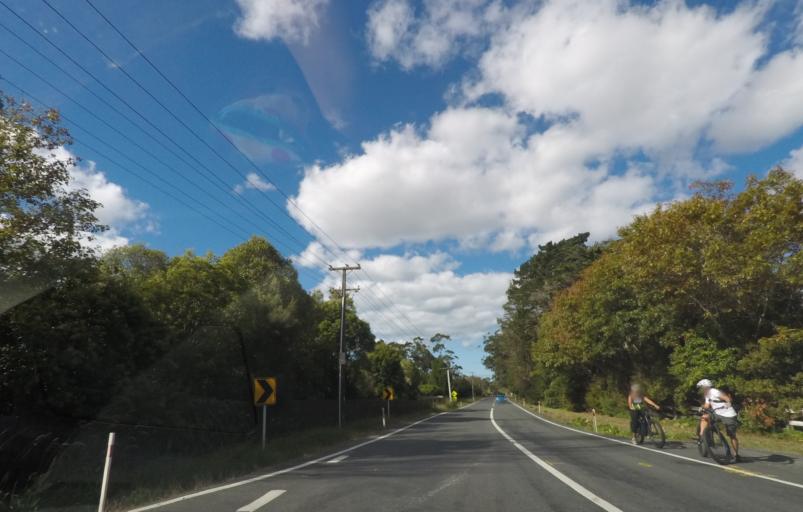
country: NZ
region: Auckland
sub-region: Auckland
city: Rothesay Bay
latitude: -36.5987
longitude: 174.6529
